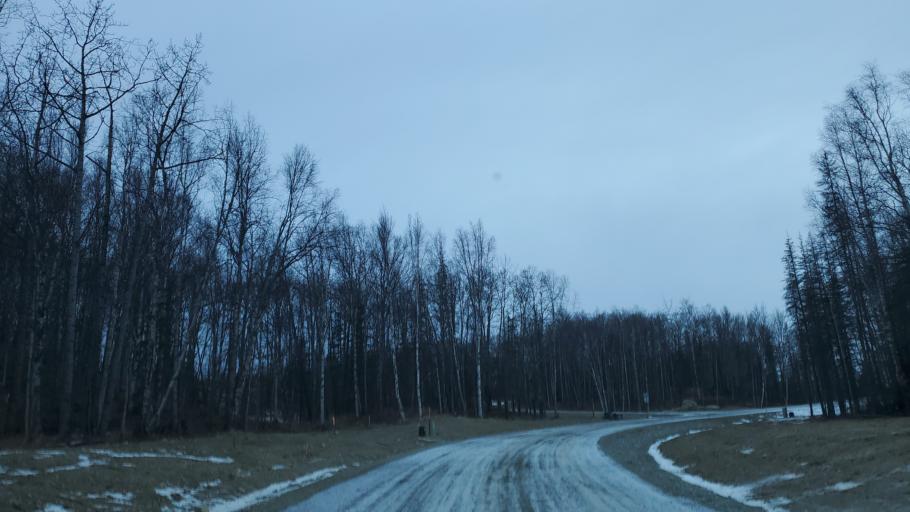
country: US
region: Alaska
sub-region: Matanuska-Susitna Borough
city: Gateway
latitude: 61.6555
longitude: -149.2340
